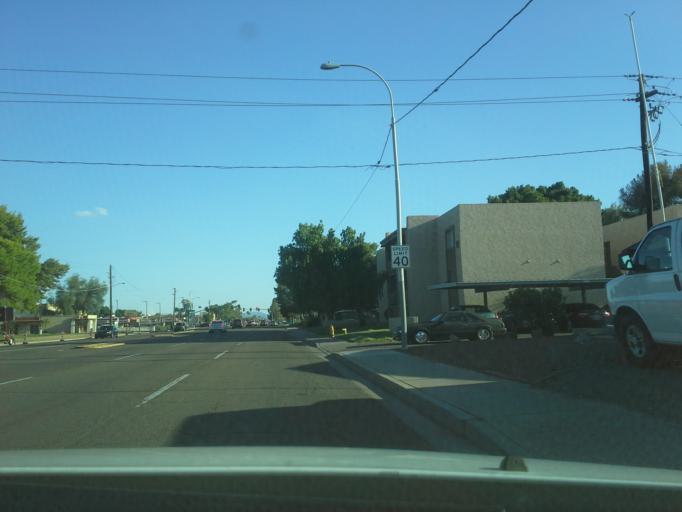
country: US
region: Arizona
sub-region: Maricopa County
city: Glendale
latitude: 33.5734
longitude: -112.1343
